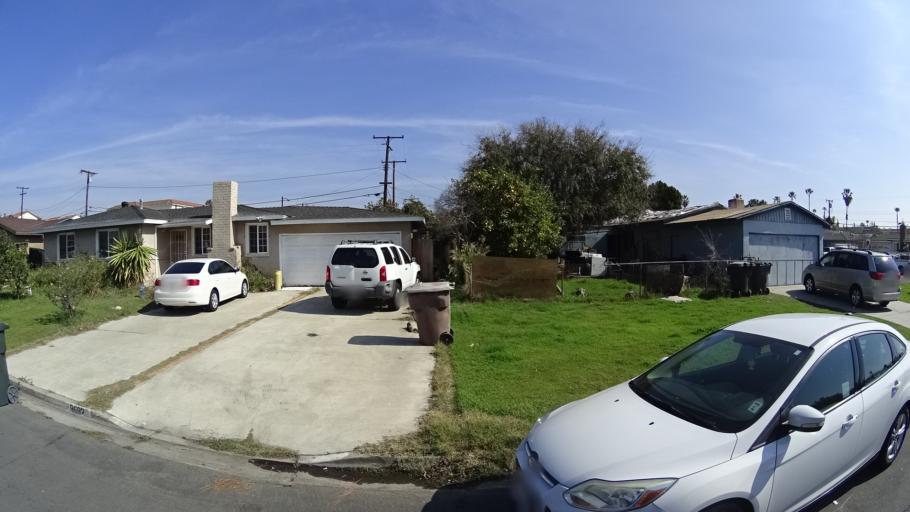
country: US
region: California
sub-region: Orange County
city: Stanton
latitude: 33.8220
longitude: -117.9608
